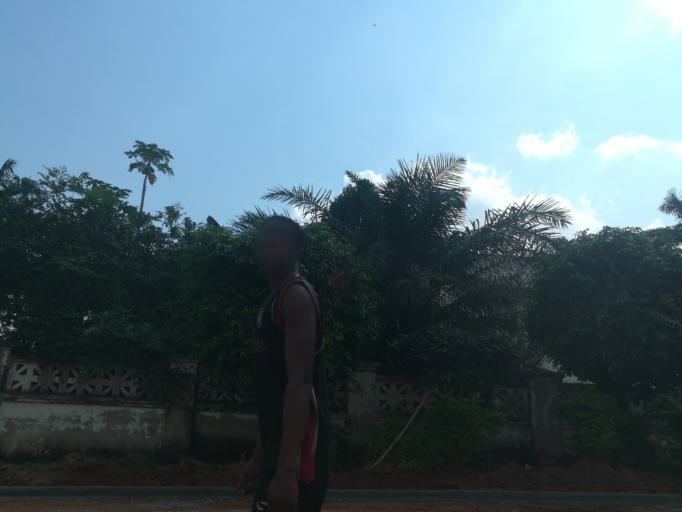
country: NG
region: Abuja Federal Capital Territory
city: Abuja
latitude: 9.0493
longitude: 7.4471
